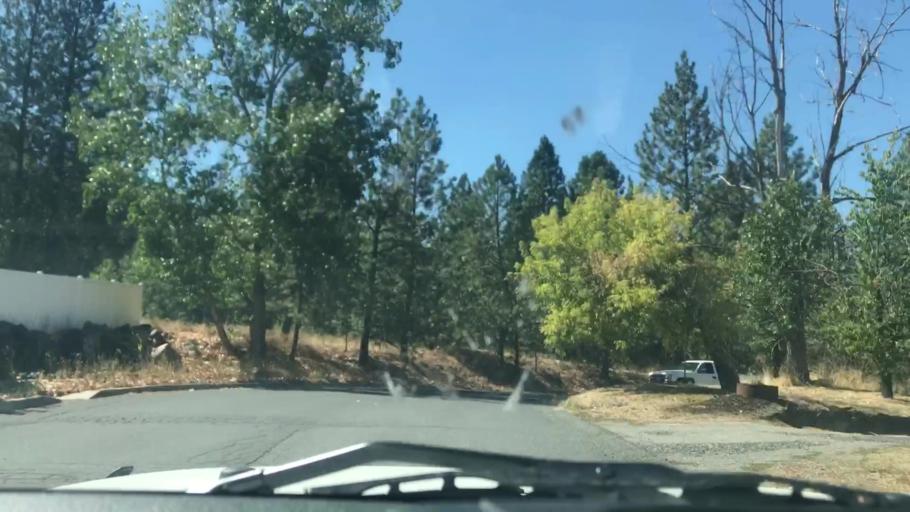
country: US
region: Washington
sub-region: Spokane County
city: Spokane
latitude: 47.6411
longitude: -117.4510
